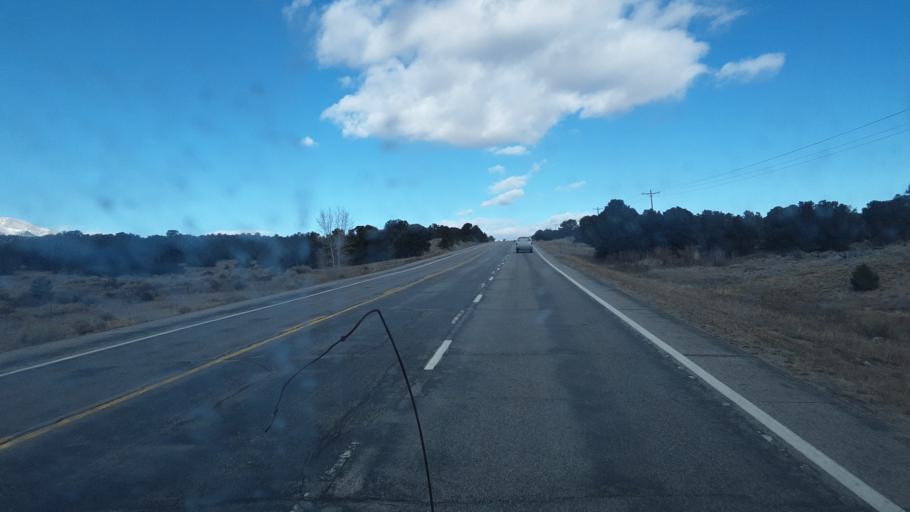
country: US
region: Colorado
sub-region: Chaffee County
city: Salida
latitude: 38.6561
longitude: -106.0863
